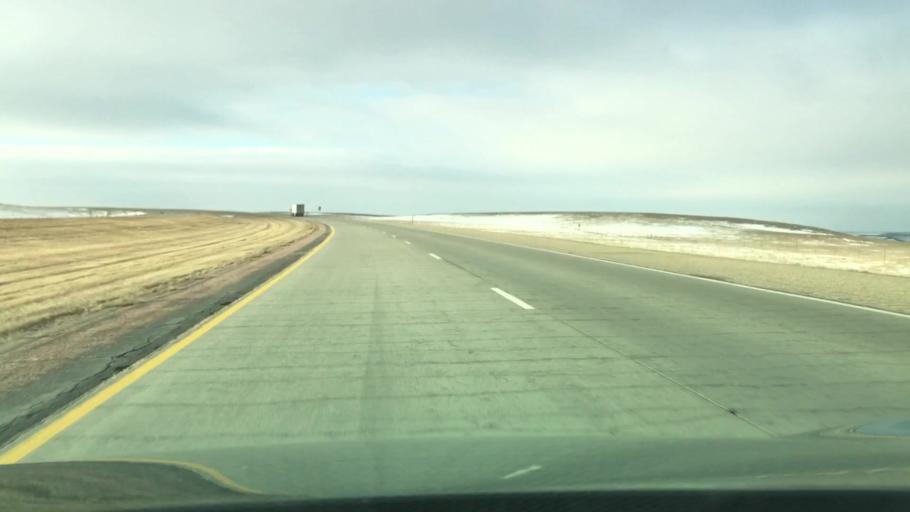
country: US
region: South Dakota
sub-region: Brule County
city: Chamberlain
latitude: 43.8418
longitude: -99.4828
